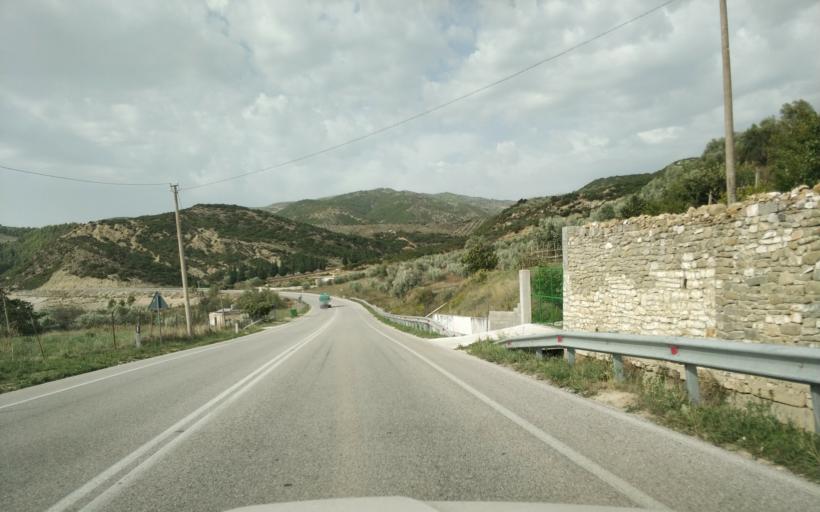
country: AL
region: Gjirokaster
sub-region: Rrethi i Tepelenes
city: Memaliaj
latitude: 40.3764
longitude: 19.9061
